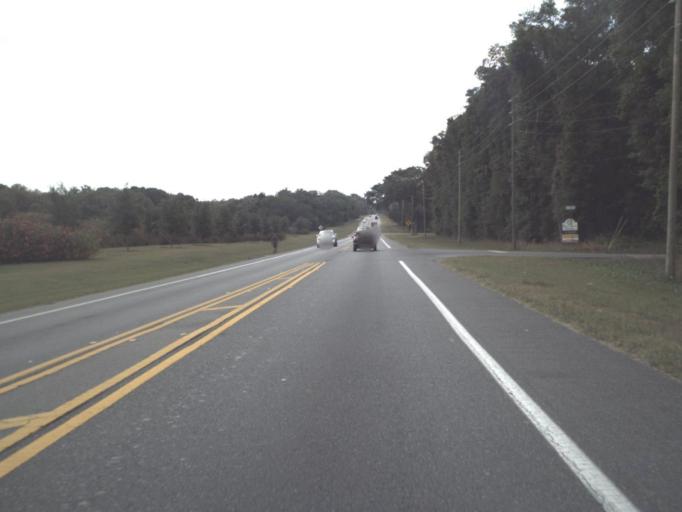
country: US
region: Florida
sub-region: Marion County
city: Ocala
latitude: 29.2595
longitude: -82.1402
